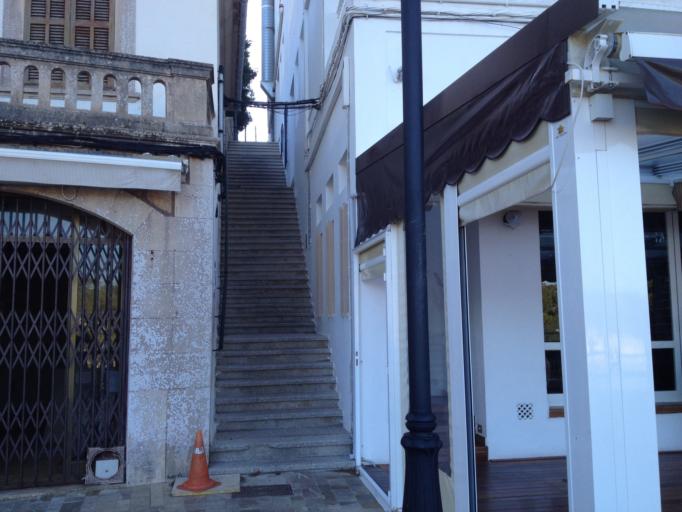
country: ES
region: Balearic Islands
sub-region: Illes Balears
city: Santanyi
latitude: 39.3304
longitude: 3.1713
